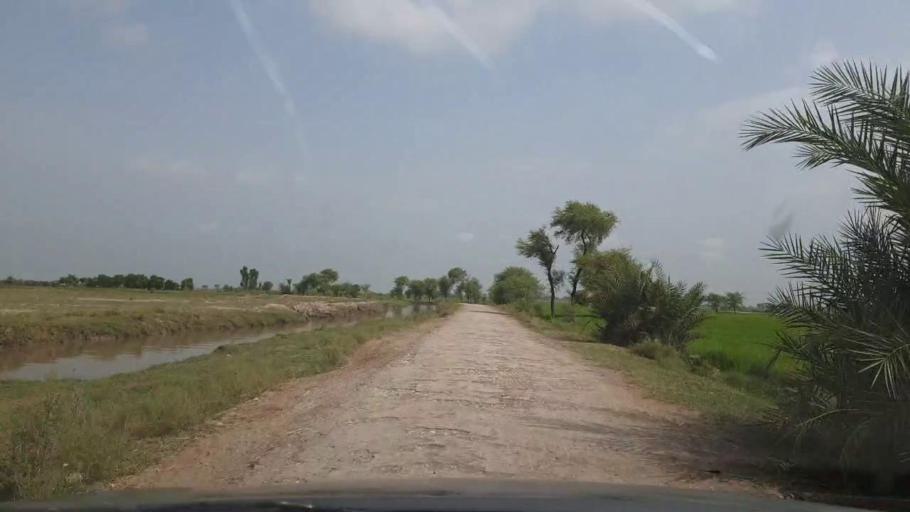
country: PK
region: Sindh
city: Ratodero
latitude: 27.8444
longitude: 68.3080
